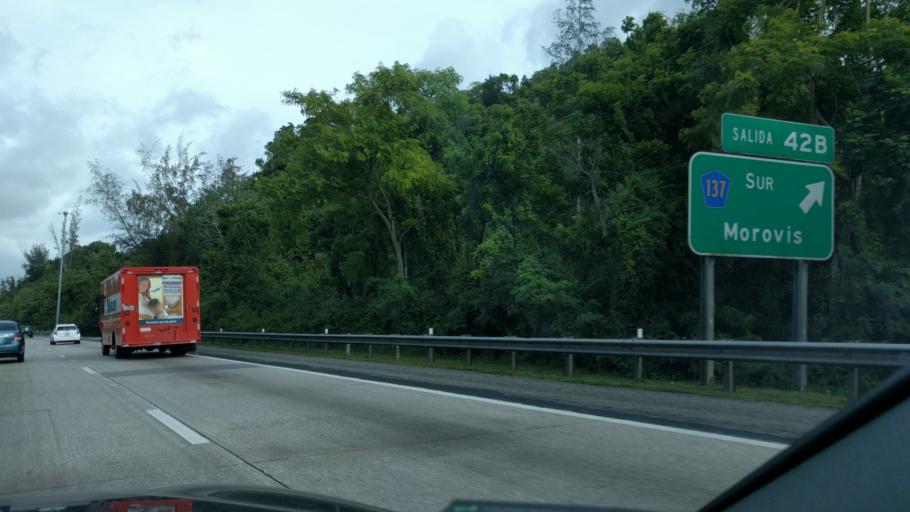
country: PR
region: Vega Baja
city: Coto Norte
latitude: 18.4384
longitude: -66.4315
